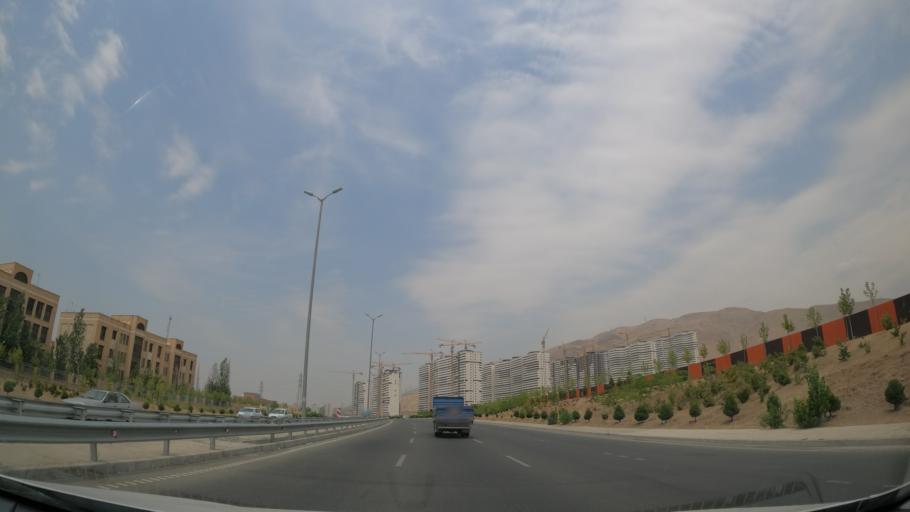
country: IR
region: Tehran
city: Shahr-e Qods
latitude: 35.7513
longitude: 51.1692
